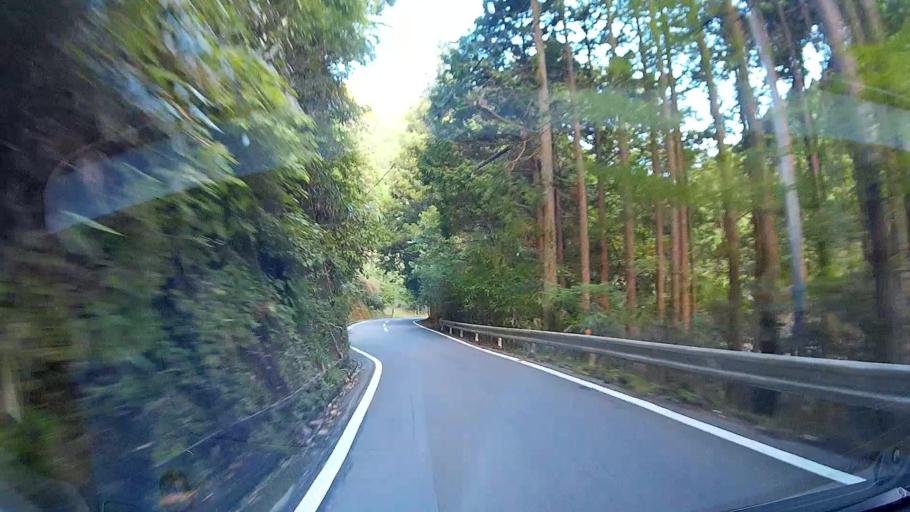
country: JP
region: Shizuoka
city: Shizuoka-shi
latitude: 35.1485
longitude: 138.2663
